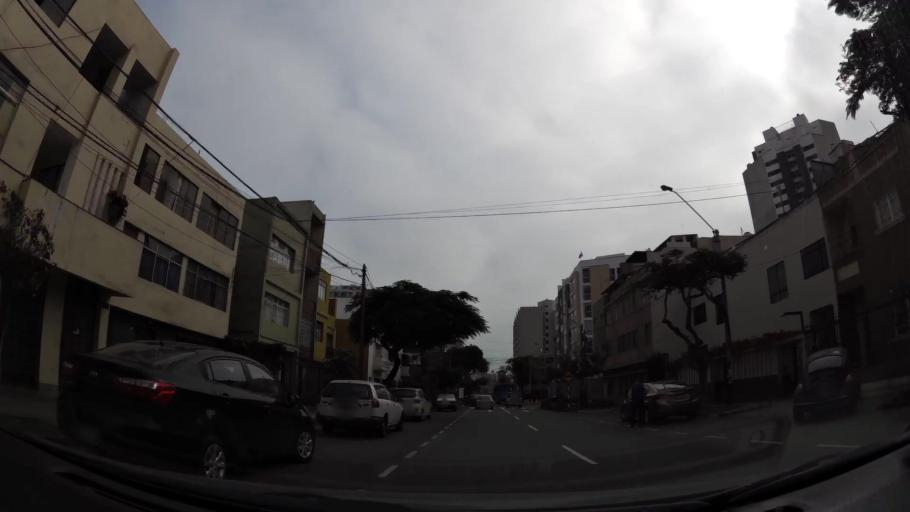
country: PE
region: Lima
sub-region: Lima
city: San Isidro
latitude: -12.0839
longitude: -77.0454
